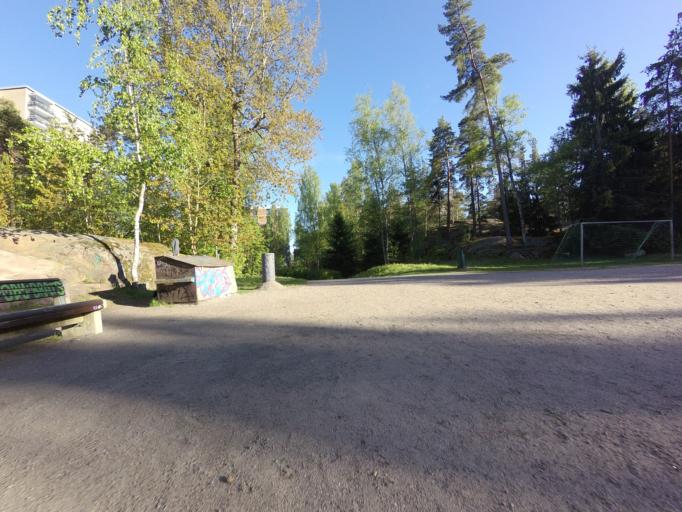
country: FI
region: Uusimaa
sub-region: Helsinki
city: Kauniainen
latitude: 60.1760
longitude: 24.7230
